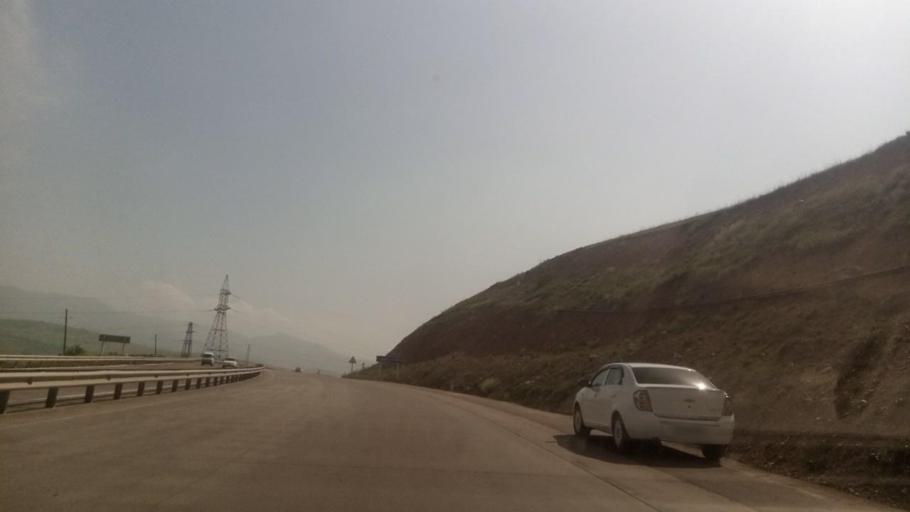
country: UZ
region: Toshkent
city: Angren
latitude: 41.0705
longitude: 70.2326
